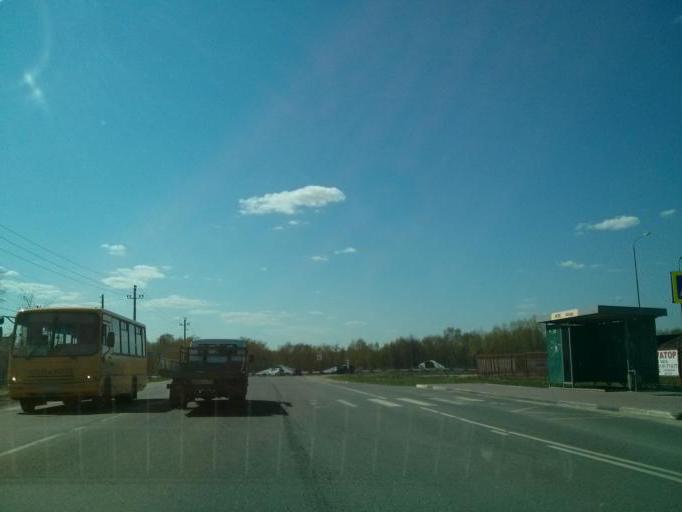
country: RU
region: Nizjnij Novgorod
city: Taremskoye
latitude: 55.9340
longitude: 43.0470
